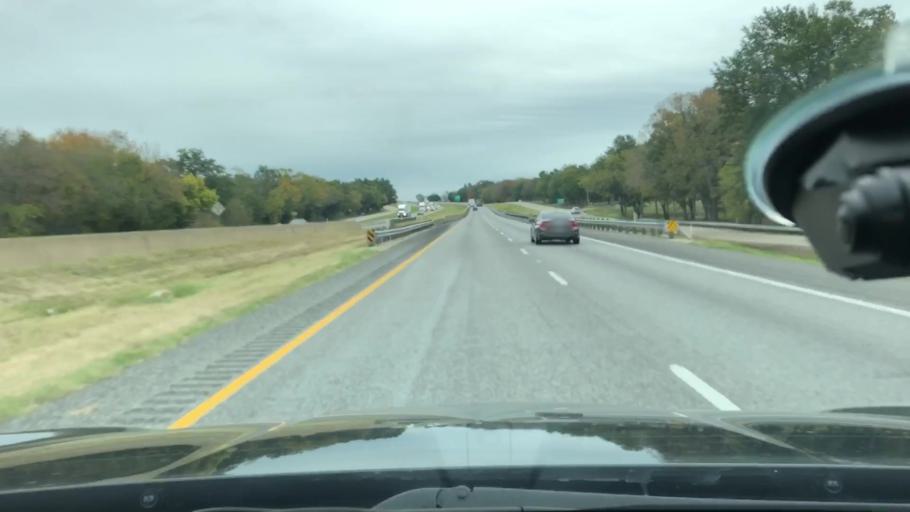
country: US
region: Texas
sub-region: Hunt County
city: Greenville
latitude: 33.1289
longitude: -95.9788
